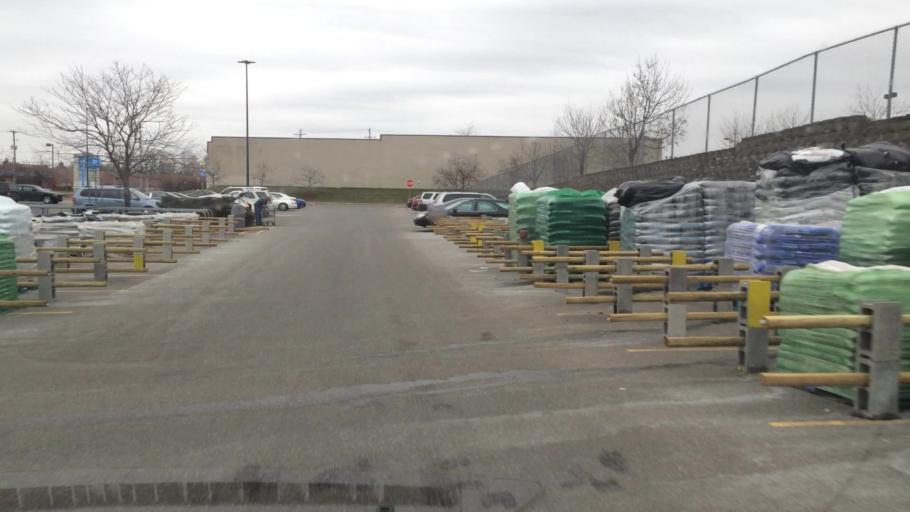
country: US
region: Ohio
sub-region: Summit County
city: Silver Lake
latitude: 41.1653
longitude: -81.4789
